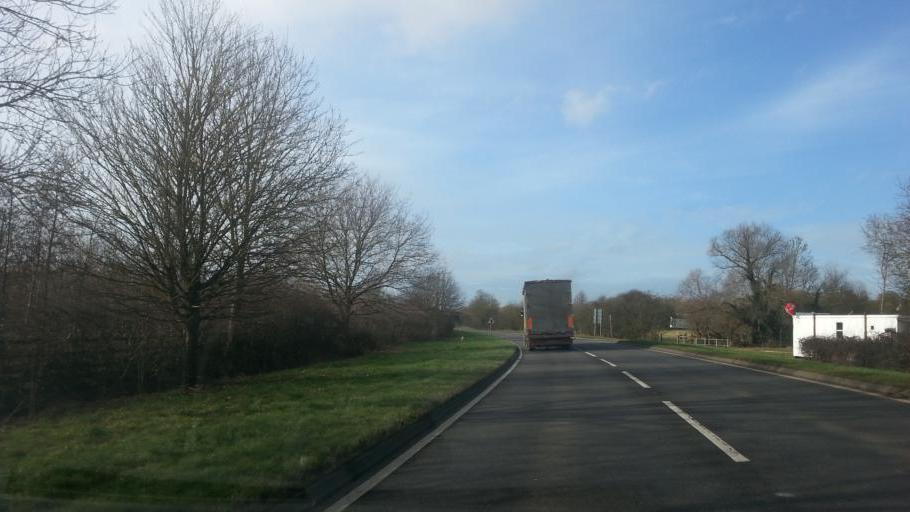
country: GB
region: England
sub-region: District of Rutland
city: Ridlington
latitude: 52.5966
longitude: -0.7868
